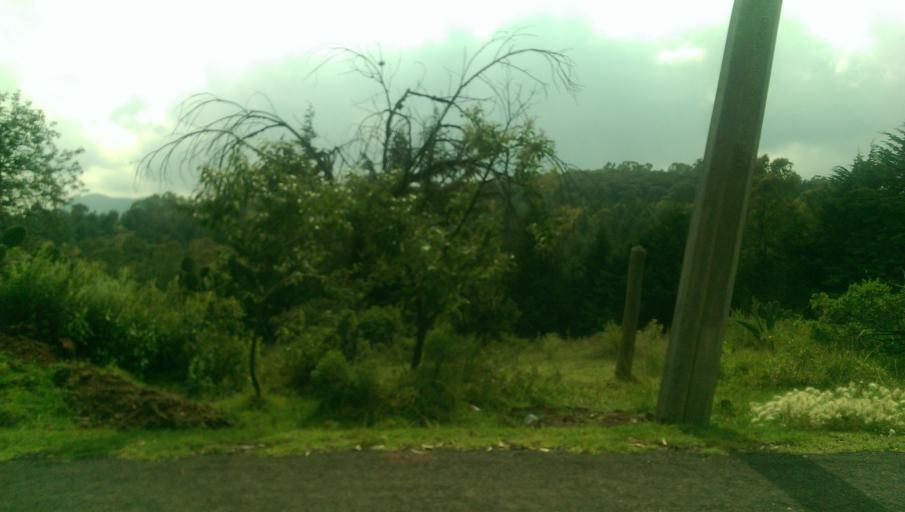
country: MX
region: Mexico
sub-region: Jilotepec
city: Jilotepec de Molina Enriquez
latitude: 19.9437
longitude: -99.4906
